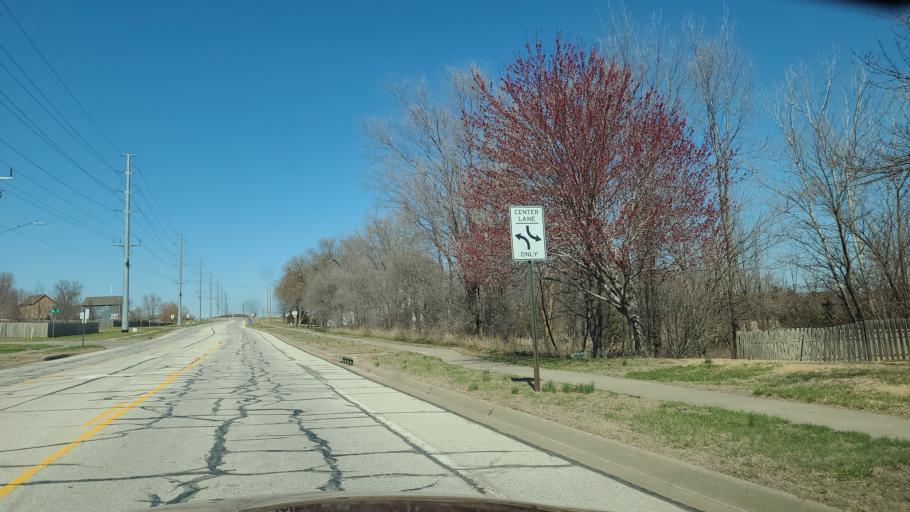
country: US
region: Kansas
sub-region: Douglas County
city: Lawrence
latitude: 38.9353
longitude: -95.2048
